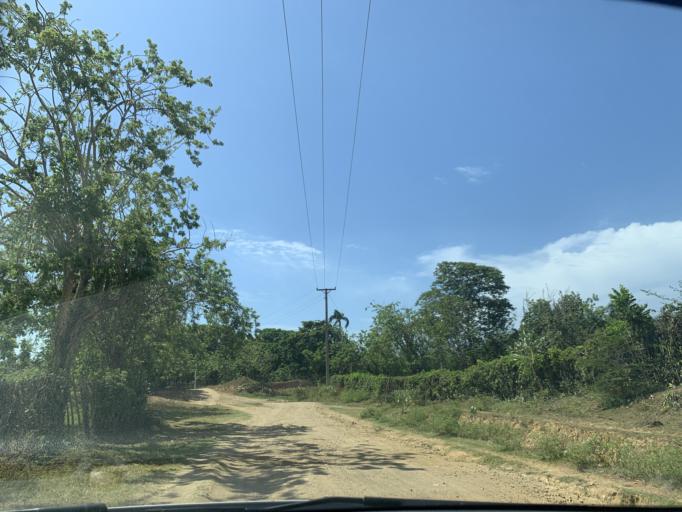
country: DO
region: Puerto Plata
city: Luperon
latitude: 19.8856
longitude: -70.8733
